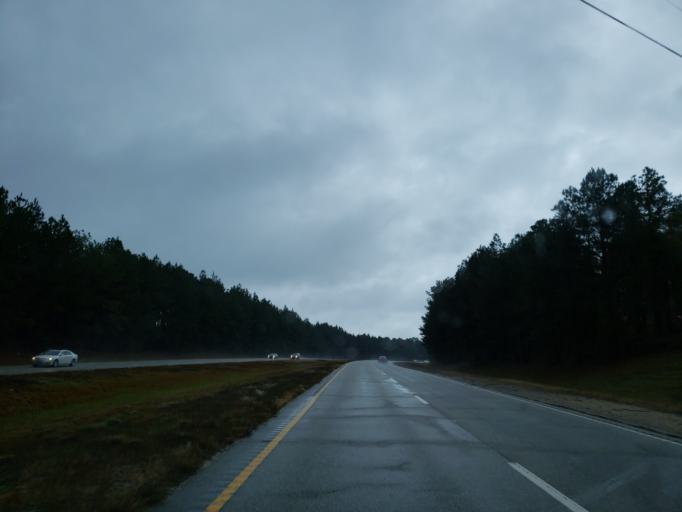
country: US
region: Mississippi
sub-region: Lauderdale County
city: Meridian
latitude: 32.2811
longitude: -88.6972
